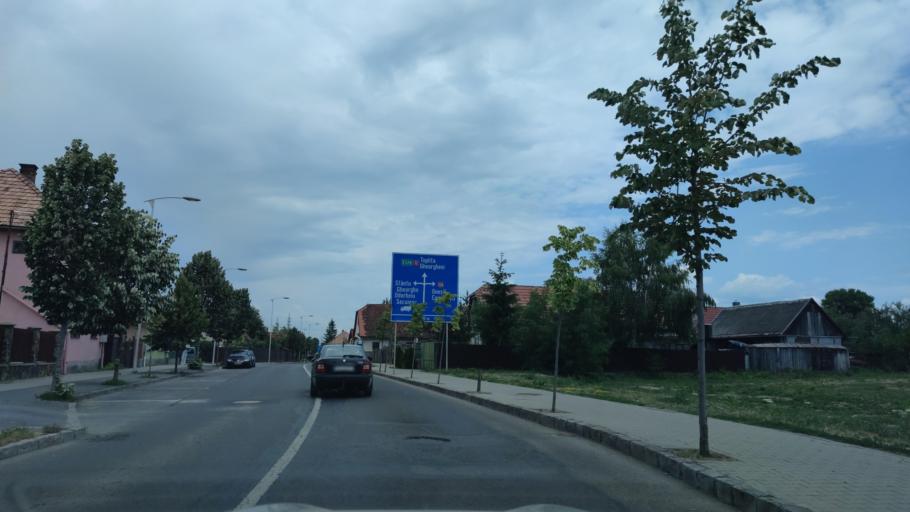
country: RO
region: Harghita
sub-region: Municipiul Miercurea Ciuc
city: Miercurea-Ciuc
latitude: 46.3784
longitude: 25.8018
